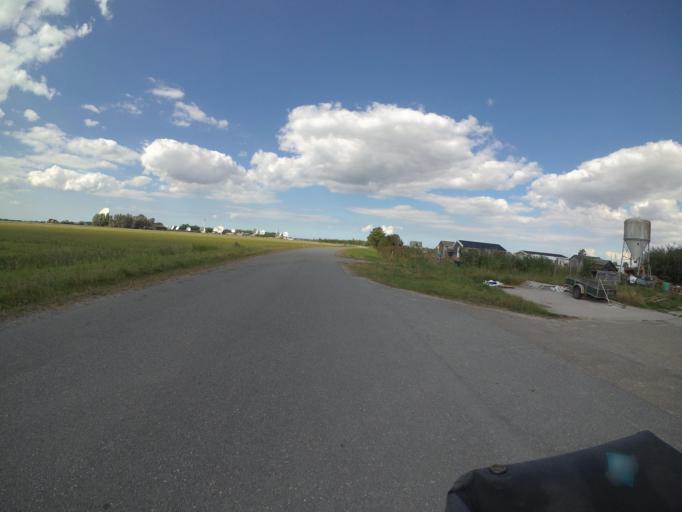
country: NL
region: Friesland
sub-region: Gemeente Kollumerland en Nieuwkruisland
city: Kollum
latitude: 53.2789
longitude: 6.2223
